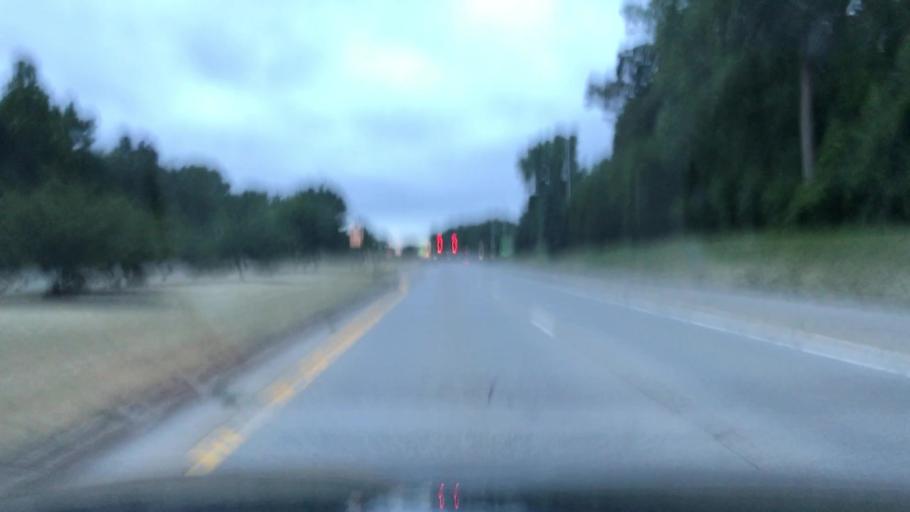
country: US
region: Michigan
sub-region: Kent County
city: East Grand Rapids
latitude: 42.9599
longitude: -85.5902
